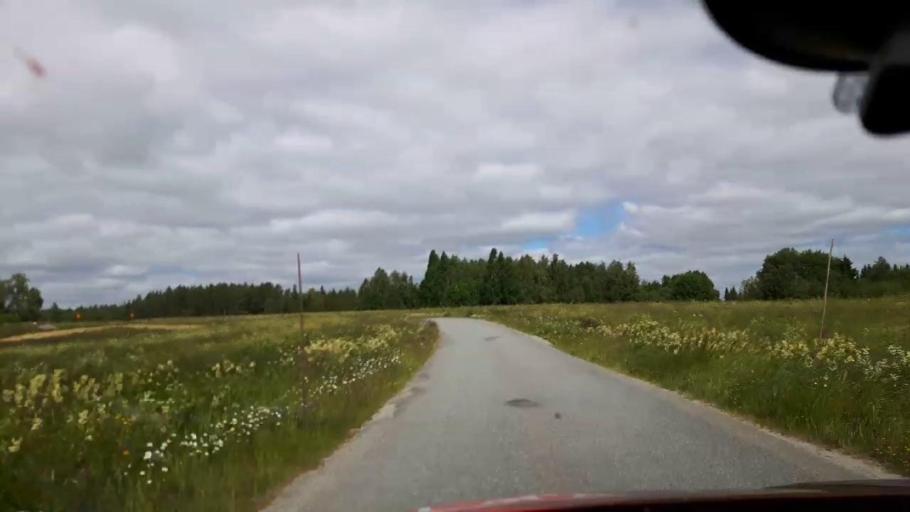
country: SE
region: Jaemtland
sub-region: Braecke Kommun
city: Braecke
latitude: 62.8511
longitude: 15.2950
